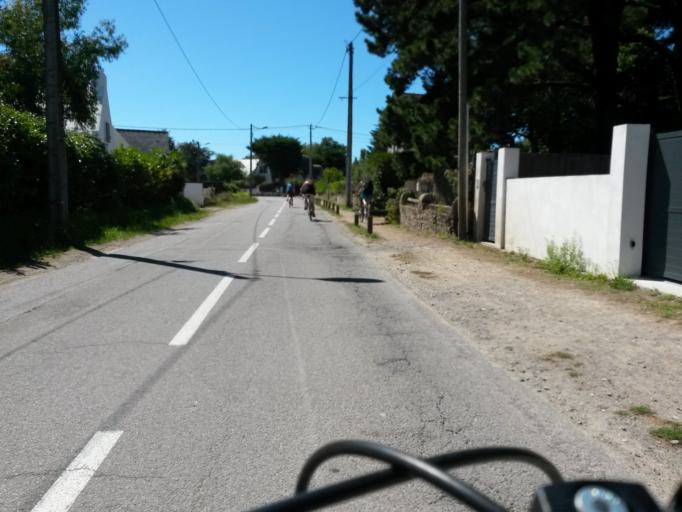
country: FR
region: Pays de la Loire
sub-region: Departement de la Loire-Atlantique
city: Mesquer
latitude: 47.4111
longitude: -2.4783
